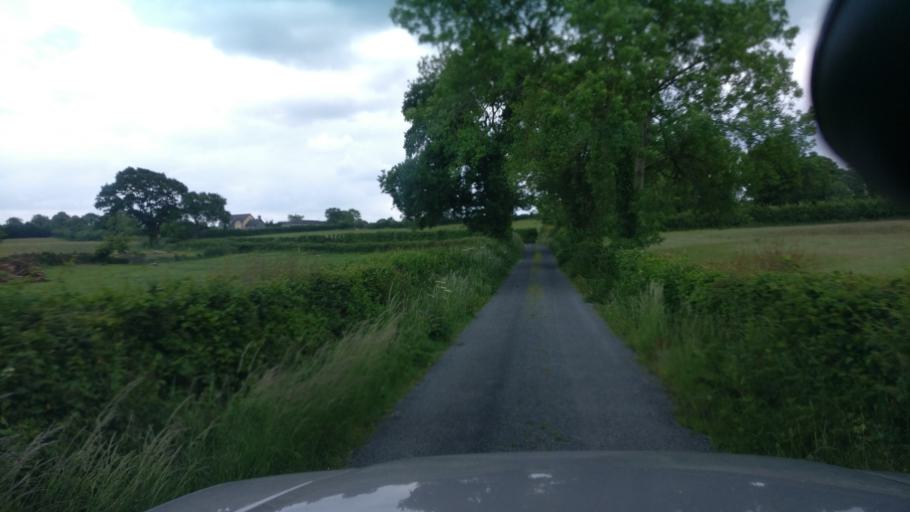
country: IE
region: Connaught
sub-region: County Galway
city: Ballinasloe
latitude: 53.3104
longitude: -8.2592
